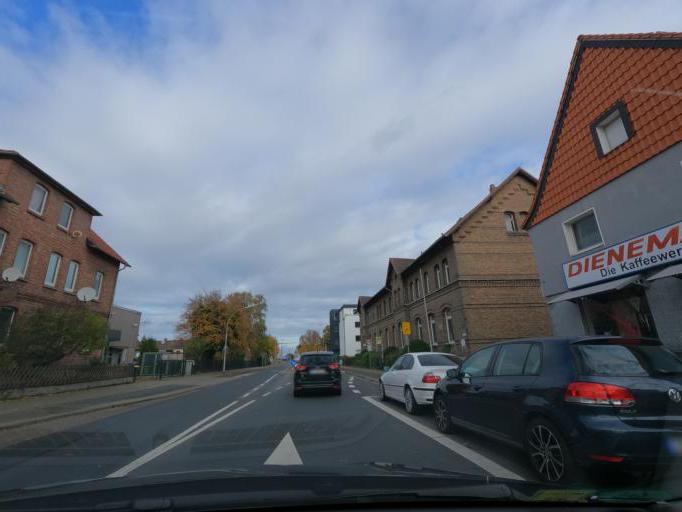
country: DE
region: Lower Saxony
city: Leiferde
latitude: 52.2225
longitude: 10.5032
